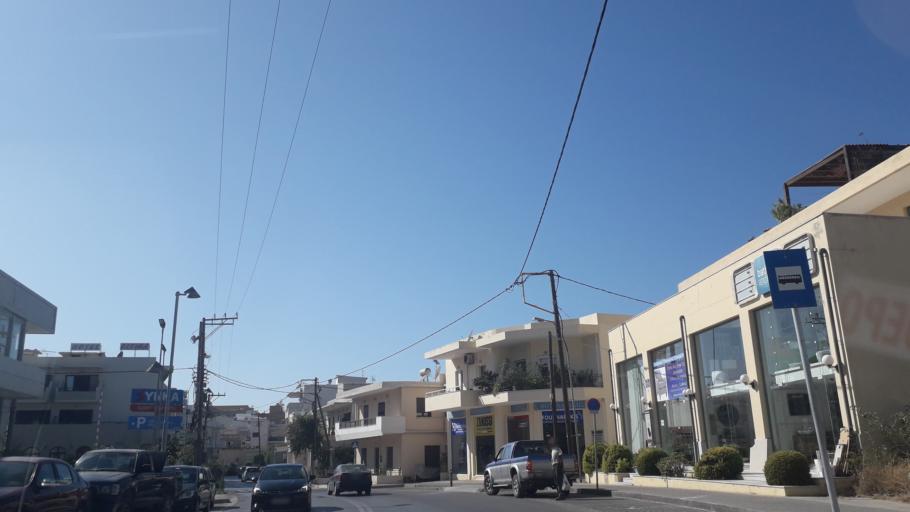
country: GR
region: Crete
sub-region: Nomos Rethymnis
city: Rethymno
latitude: 35.3658
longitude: 24.4968
